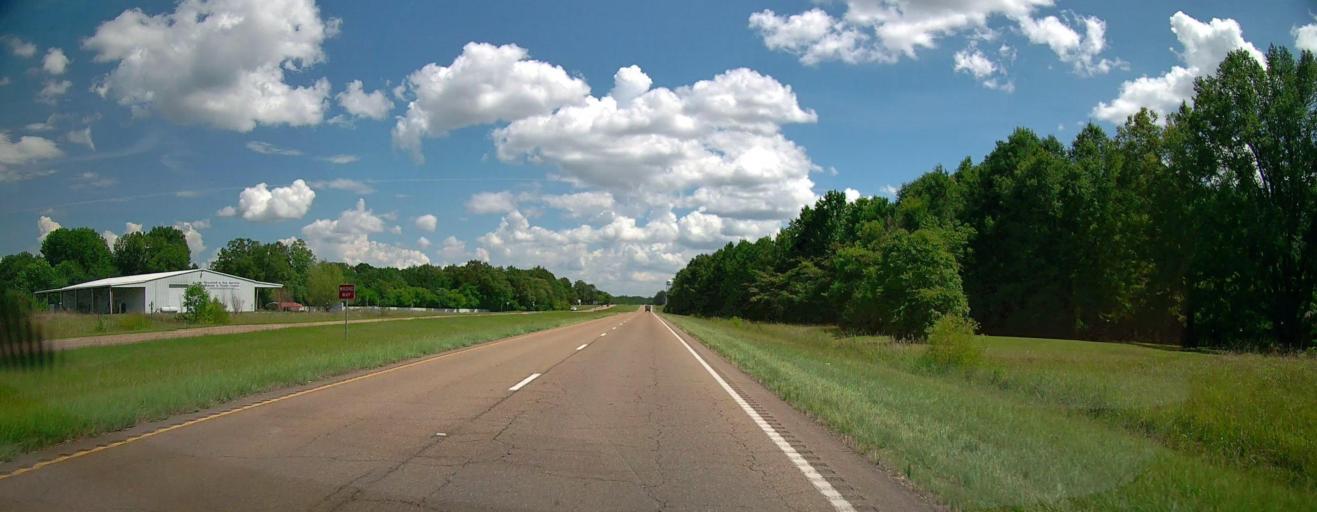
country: US
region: Mississippi
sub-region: Monroe County
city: Aberdeen
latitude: 33.8010
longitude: -88.4649
